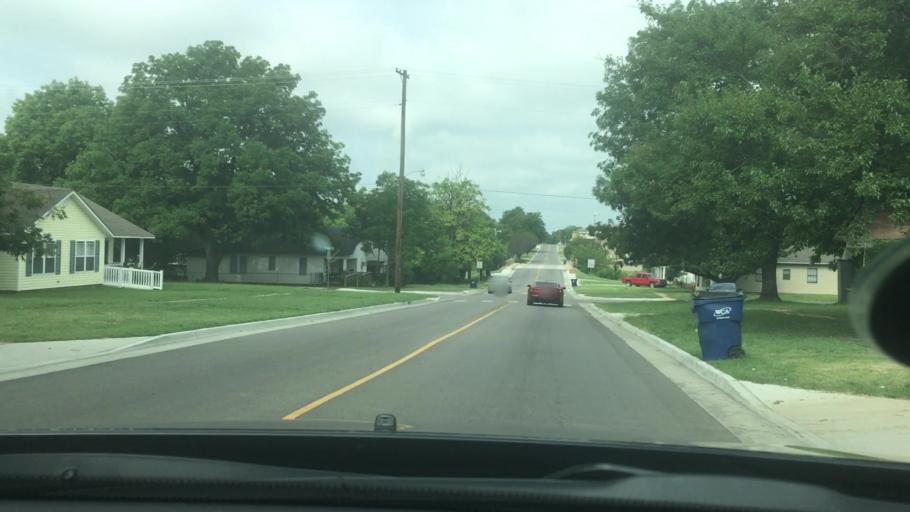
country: US
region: Oklahoma
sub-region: Pontotoc County
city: Ada
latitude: 34.7713
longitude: -96.6715
